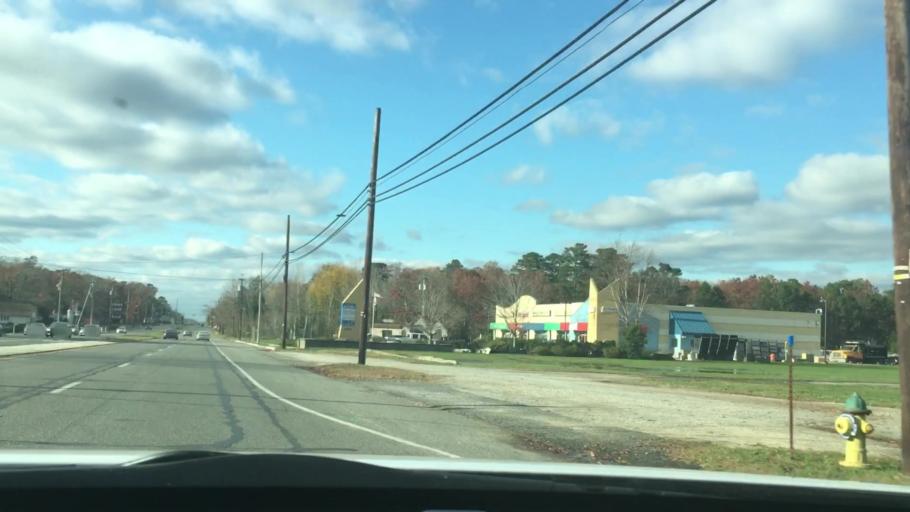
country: US
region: New Jersey
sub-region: Atlantic County
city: Pomona
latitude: 39.4219
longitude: -74.5883
